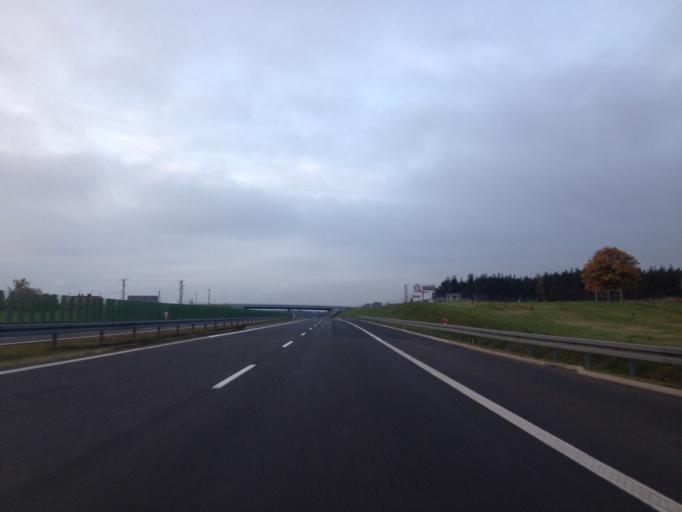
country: PL
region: Kujawsko-Pomorskie
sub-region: Powiat swiecki
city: Warlubie
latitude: 53.5808
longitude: 18.6071
